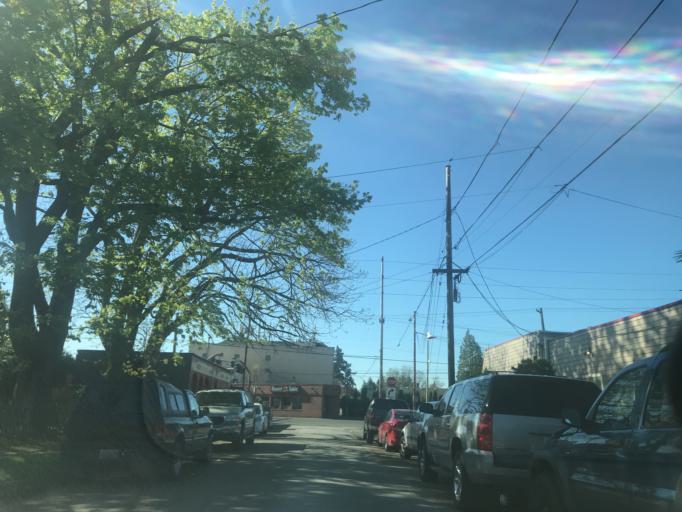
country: US
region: Oregon
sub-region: Multnomah County
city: Lents
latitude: 45.4911
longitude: -122.5983
